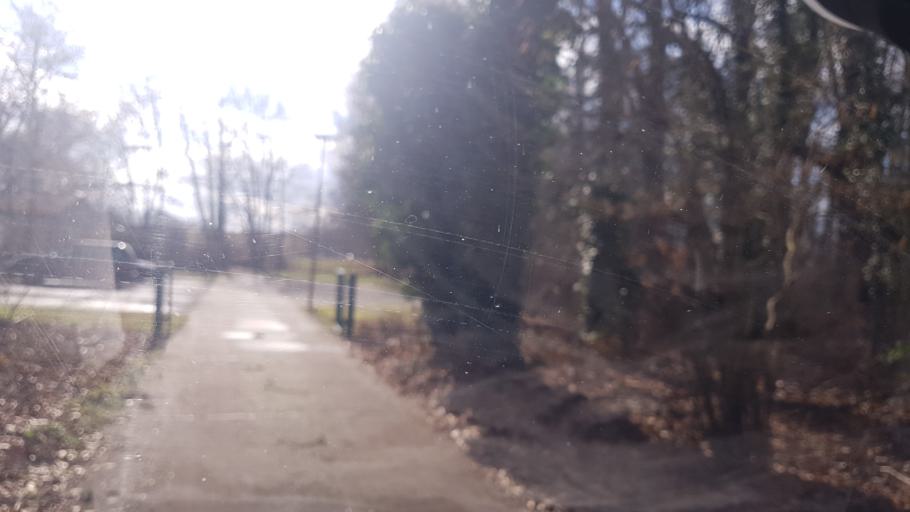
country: DE
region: Brandenburg
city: Doberlug-Kirchhain
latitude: 51.6283
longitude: 13.5625
